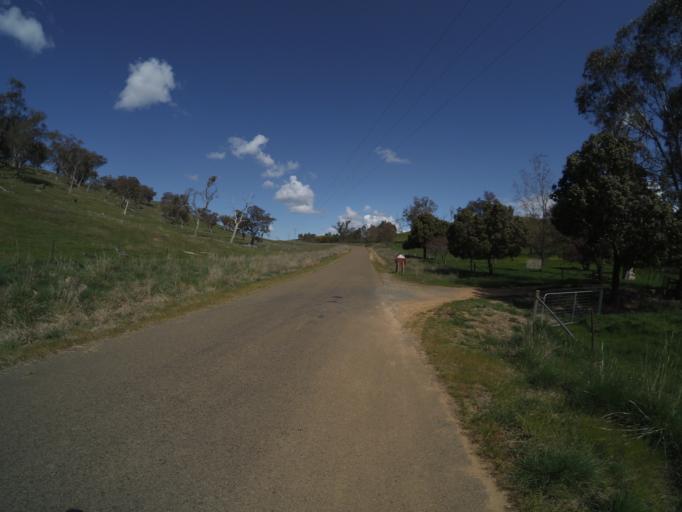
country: AU
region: New South Wales
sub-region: Yass Valley
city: Yass
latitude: -35.0255
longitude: 148.8346
